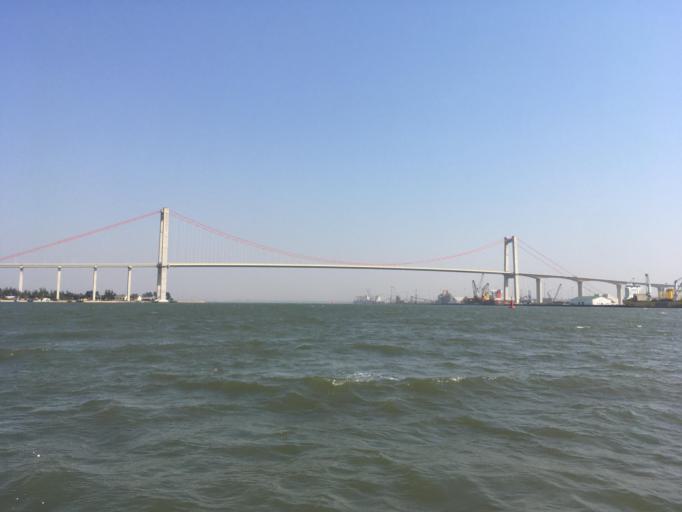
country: MZ
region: Maputo City
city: Maputo
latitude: -25.9793
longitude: 32.5648
